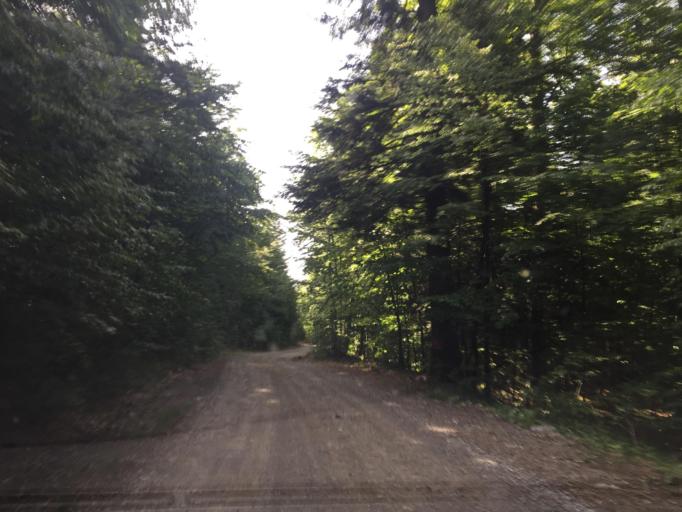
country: HR
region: Primorsko-Goranska
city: Podhum
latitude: 45.4457
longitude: 14.5558
